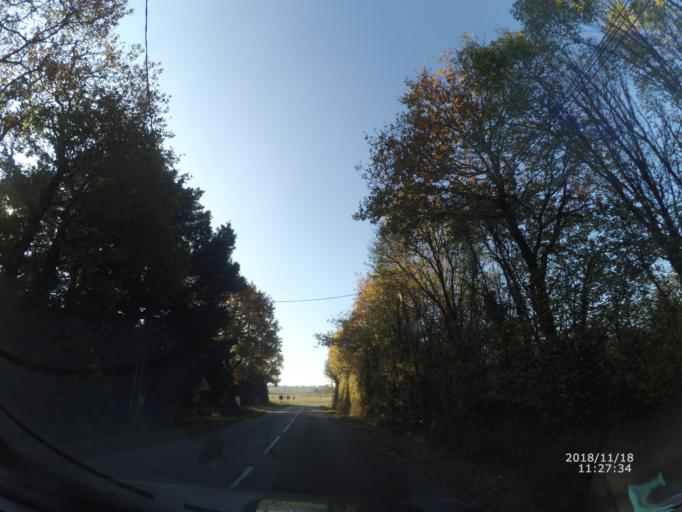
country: FR
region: Pays de la Loire
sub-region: Departement de la Loire-Atlantique
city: Saint-Michel-Chef-Chef
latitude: 47.2189
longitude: -2.1427
